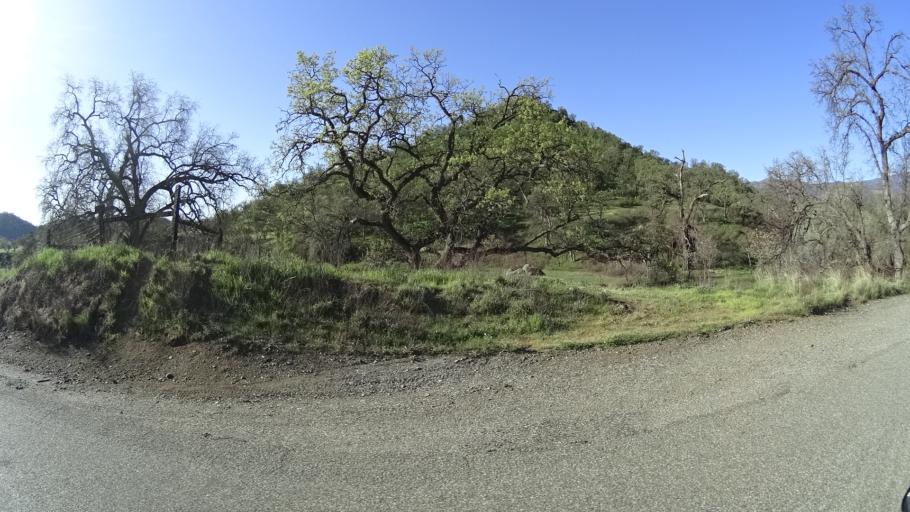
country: US
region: California
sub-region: Tehama County
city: Rancho Tehama Reserve
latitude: 39.7924
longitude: -122.5251
